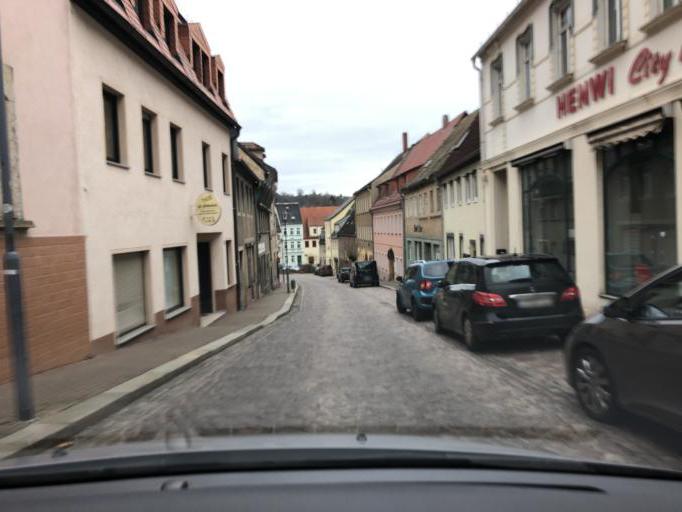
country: DE
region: Saxony
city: Rosswein
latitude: 51.0648
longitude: 13.1852
